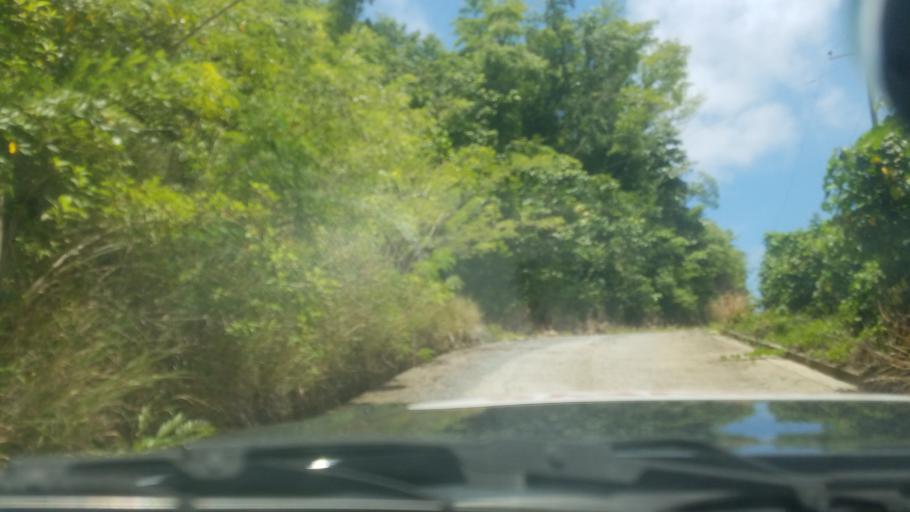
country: LC
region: Praslin
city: Praslin
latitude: 13.8693
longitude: -60.9154
